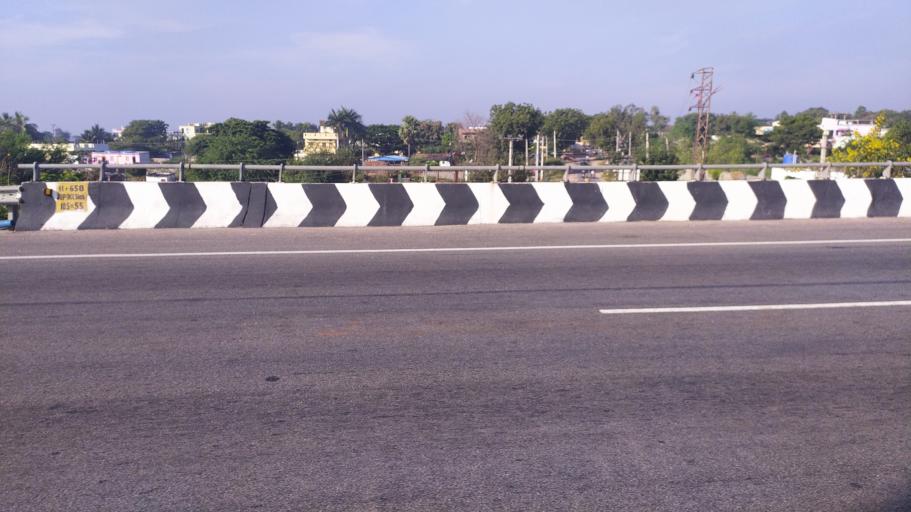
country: IN
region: Telangana
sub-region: Hyderabad
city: Hyderabad
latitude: 17.3393
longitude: 78.3660
